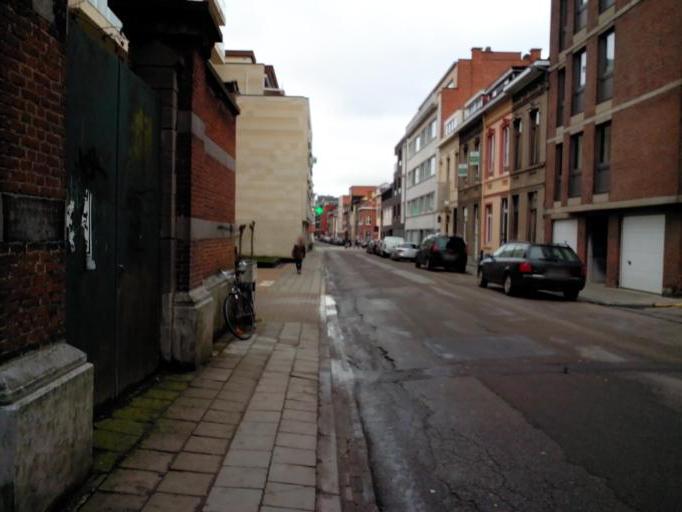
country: BE
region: Flanders
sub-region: Provincie Vlaams-Brabant
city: Leuven
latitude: 50.8715
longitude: 4.7048
